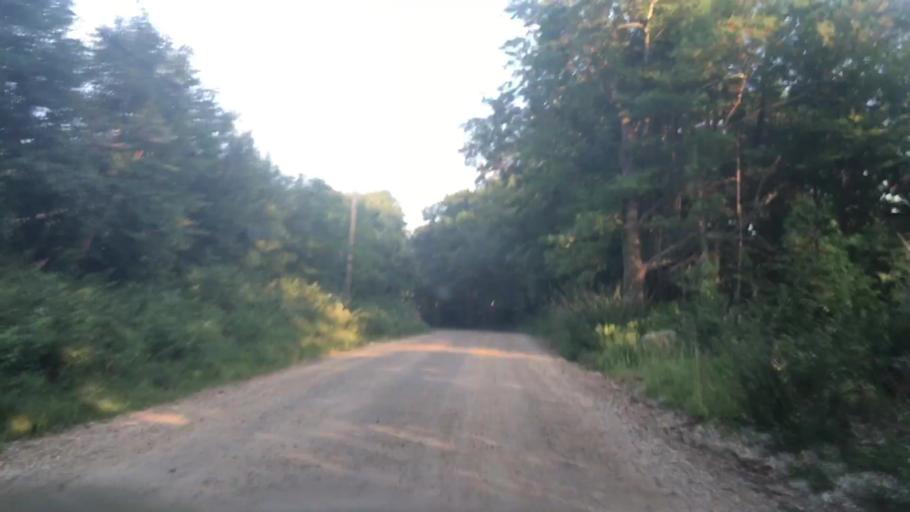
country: US
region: New Hampshire
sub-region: Belknap County
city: Barnstead
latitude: 43.4093
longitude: -71.2734
